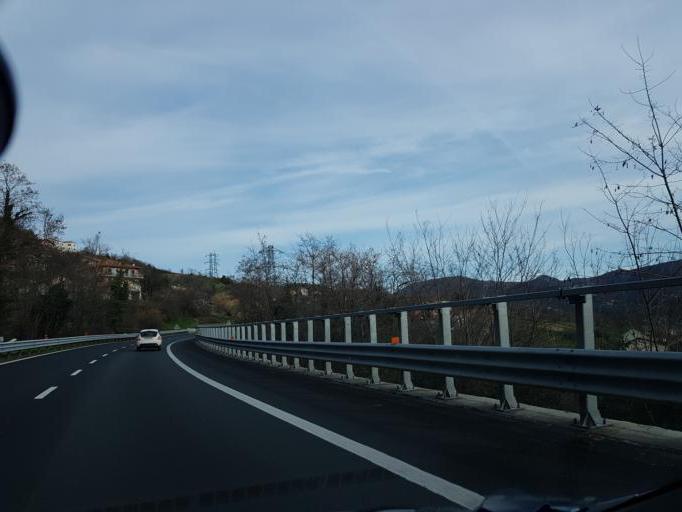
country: IT
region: Liguria
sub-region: Provincia di Genova
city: Pedemonte
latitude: 44.4997
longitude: 8.9170
